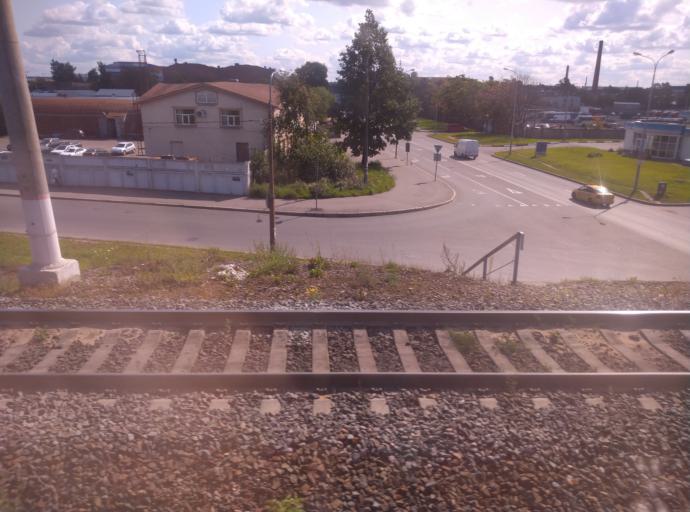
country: RU
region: St.-Petersburg
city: Centralniy
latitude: 59.9057
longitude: 30.3820
